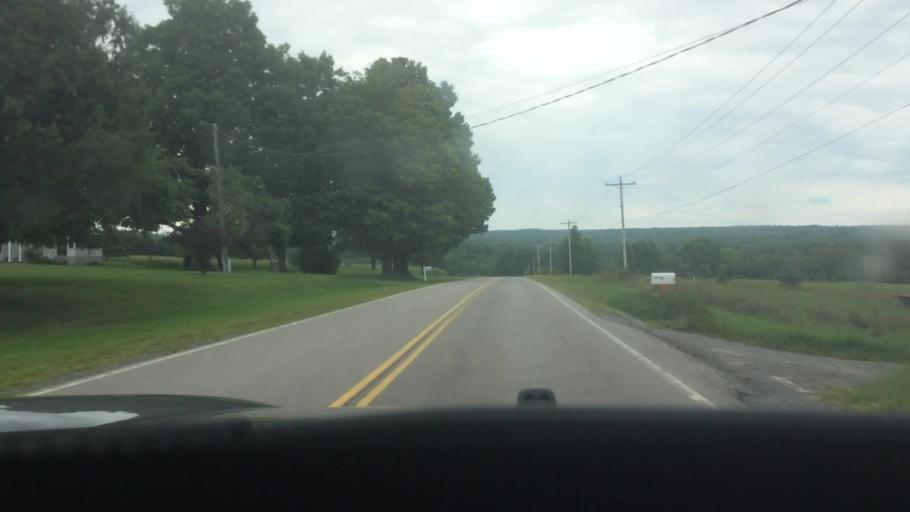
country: US
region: New York
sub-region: St. Lawrence County
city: Canton
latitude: 44.5406
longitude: -75.0822
